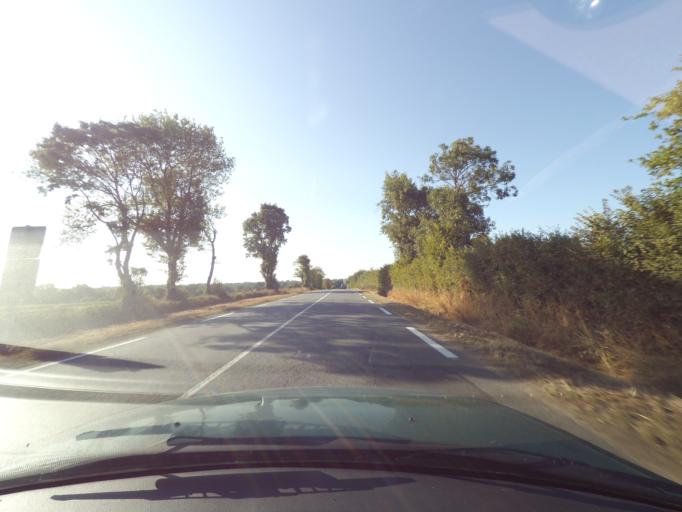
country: FR
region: Poitou-Charentes
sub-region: Departement des Deux-Sevres
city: Viennay
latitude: 46.7124
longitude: -0.2901
